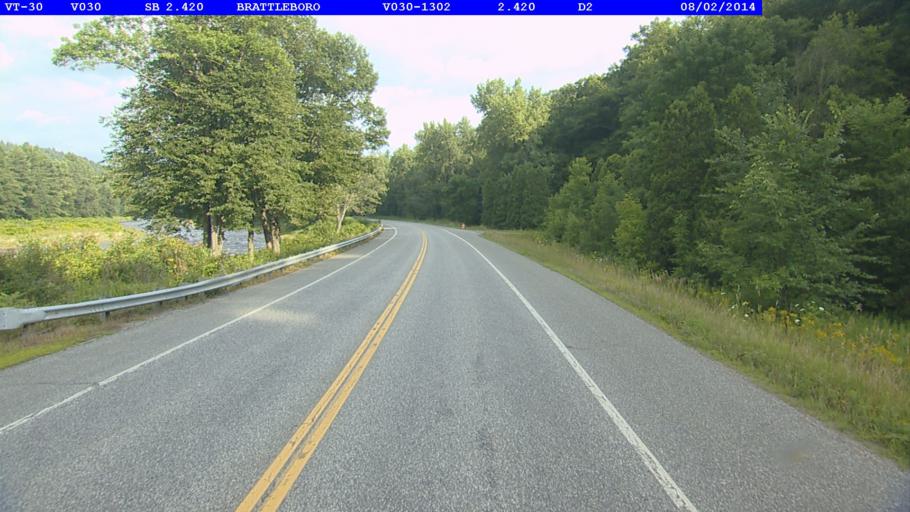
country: US
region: Vermont
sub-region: Windham County
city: West Brattleboro
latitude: 42.8837
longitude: -72.5876
